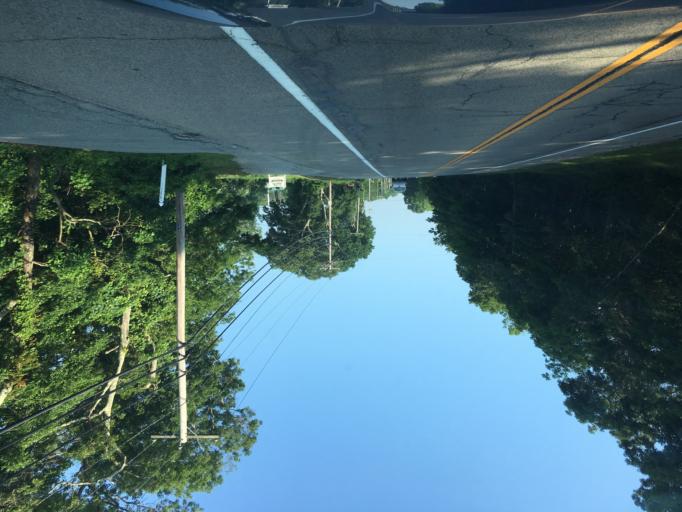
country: US
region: Rhode Island
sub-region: Washington County
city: Exeter
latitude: 41.5300
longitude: -71.5492
